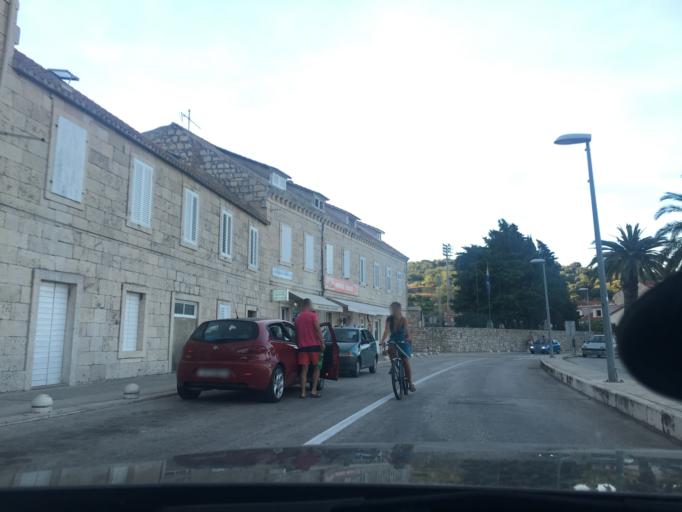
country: HR
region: Splitsko-Dalmatinska
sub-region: Grad Vis
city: Vis
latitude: 43.0624
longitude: 16.1839
